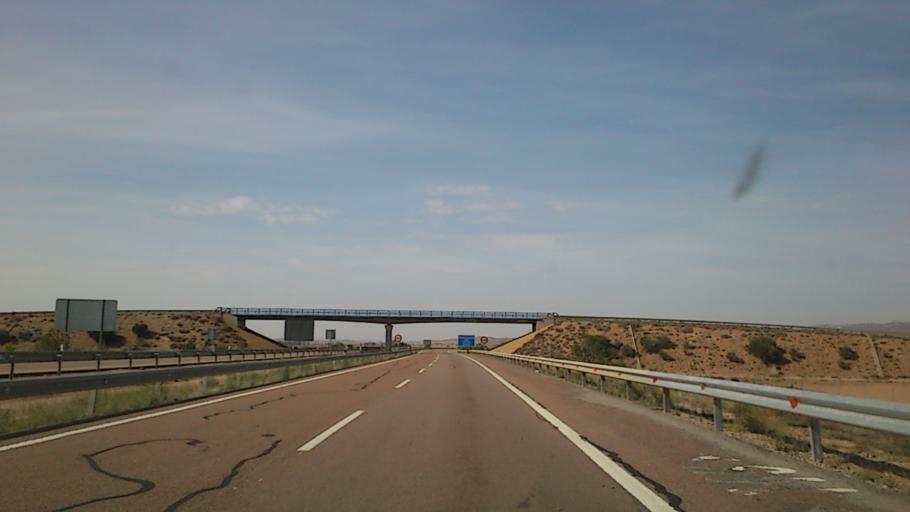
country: ES
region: Aragon
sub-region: Provincia de Teruel
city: Santa Eulalia
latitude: 40.5724
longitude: -1.2811
